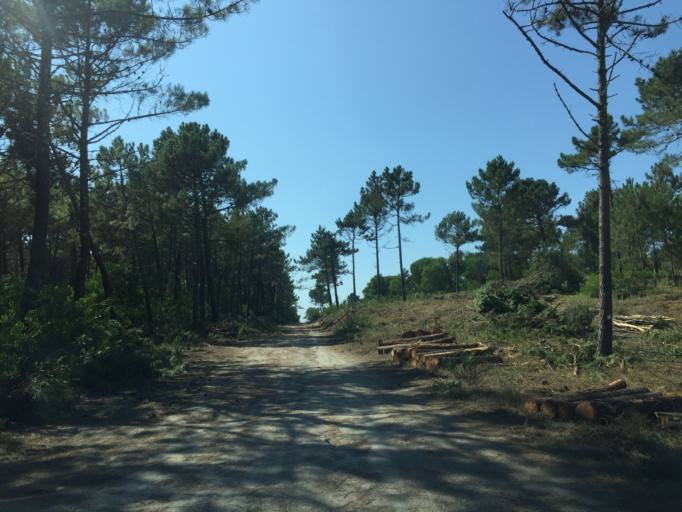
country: PT
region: Coimbra
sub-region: Figueira da Foz
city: Tavarede
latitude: 40.2624
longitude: -8.8592
